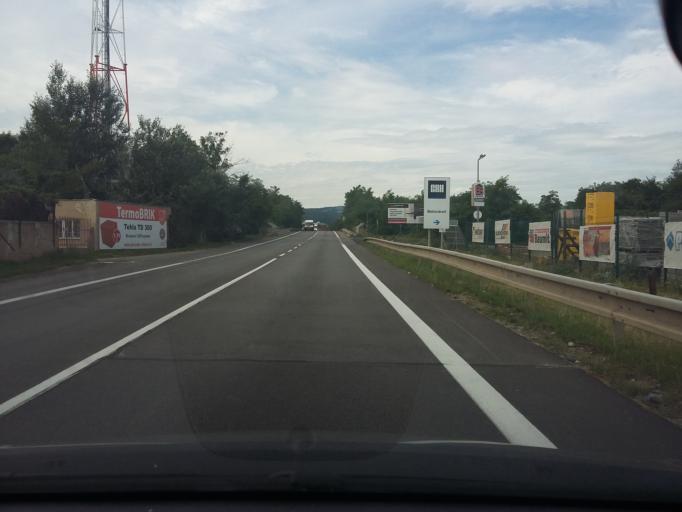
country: SK
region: Bratislavsky
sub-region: Okres Pezinok
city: Pezinok
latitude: 48.2867
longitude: 17.2827
